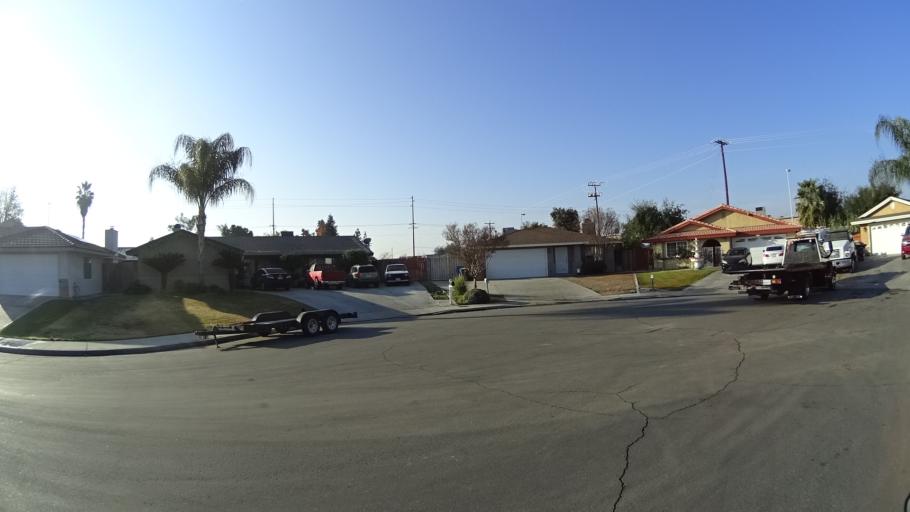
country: US
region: California
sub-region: Kern County
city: Greenfield
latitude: 35.2972
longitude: -119.0251
